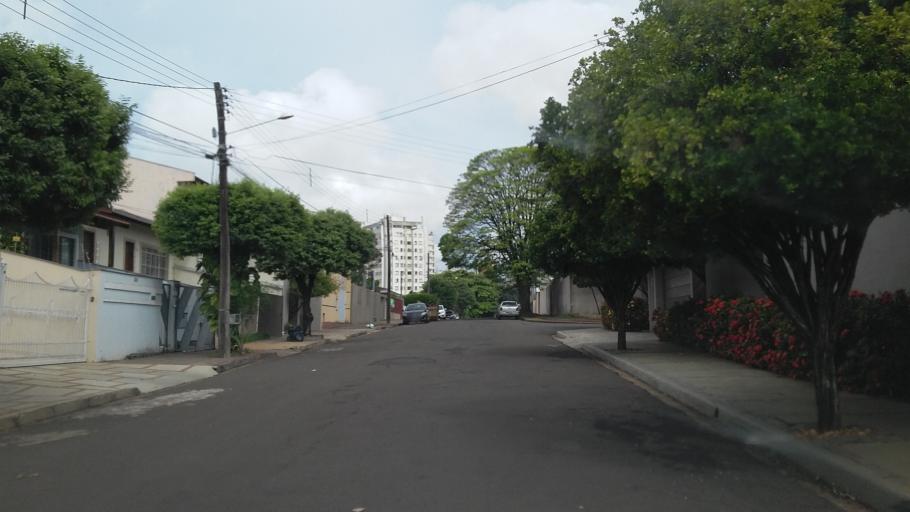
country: BR
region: Parana
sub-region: Londrina
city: Londrina
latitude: -23.3053
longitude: -51.1730
